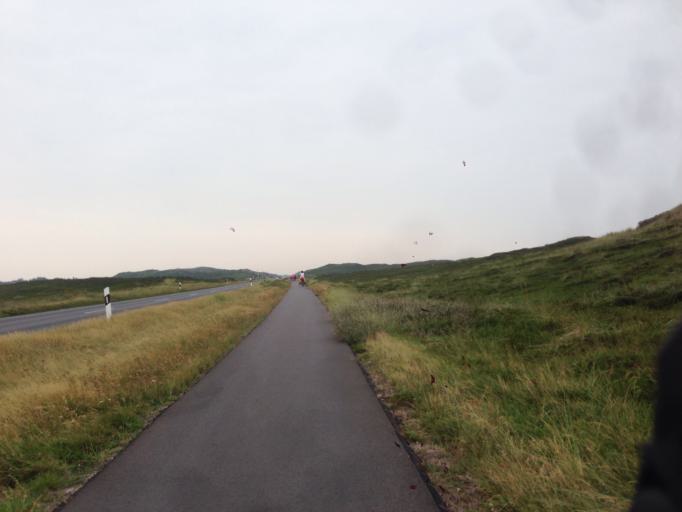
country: DE
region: Schleswig-Holstein
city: Westerland
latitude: 54.8082
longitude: 8.2881
